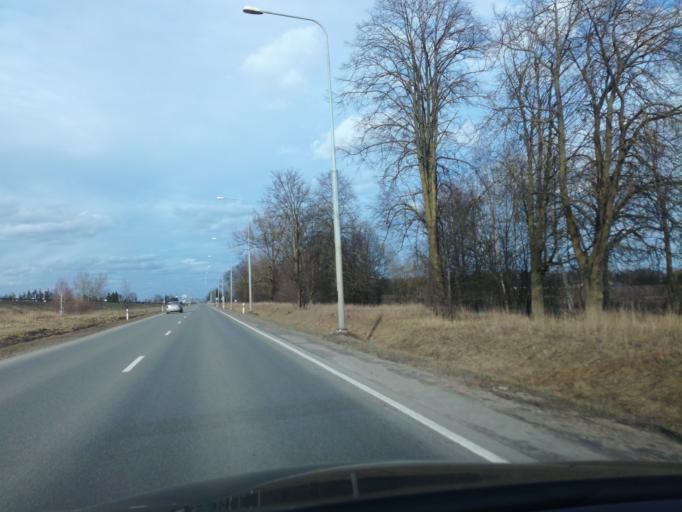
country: LT
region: Marijampoles apskritis
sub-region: Marijampole Municipality
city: Marijampole
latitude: 54.5833
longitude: 23.3792
